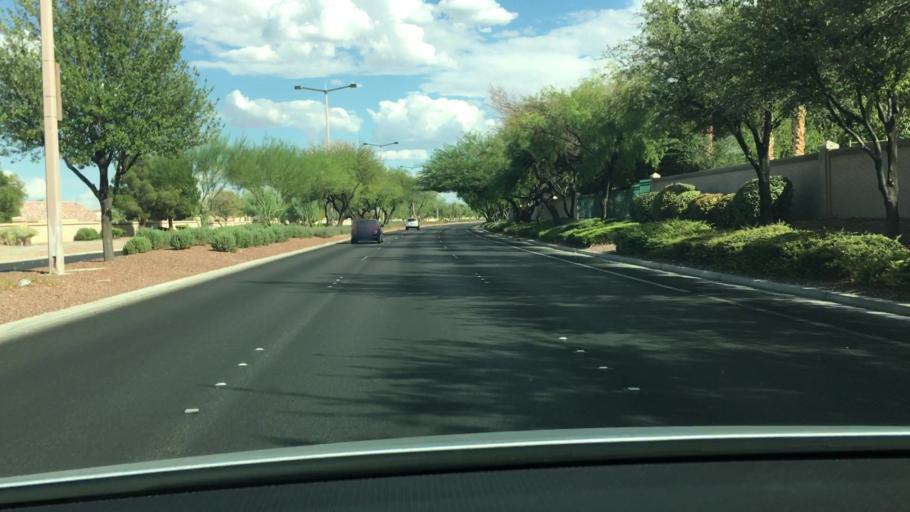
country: US
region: Nevada
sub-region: Clark County
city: Summerlin South
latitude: 36.2043
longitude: -115.2904
